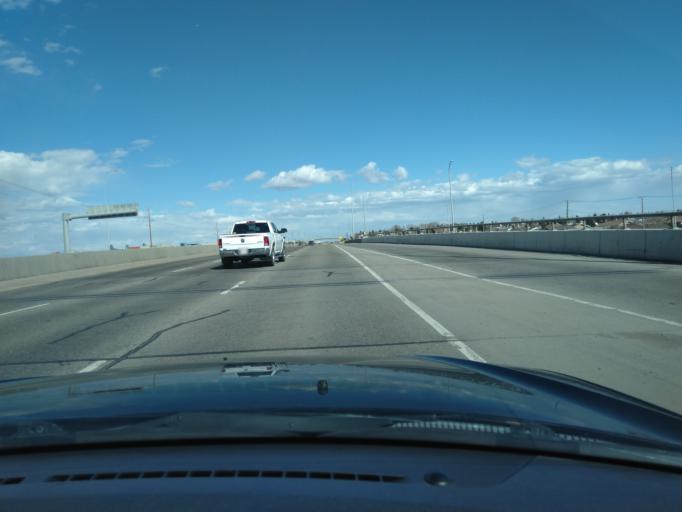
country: CA
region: Alberta
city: Calgary
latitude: 51.0957
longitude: -113.9825
